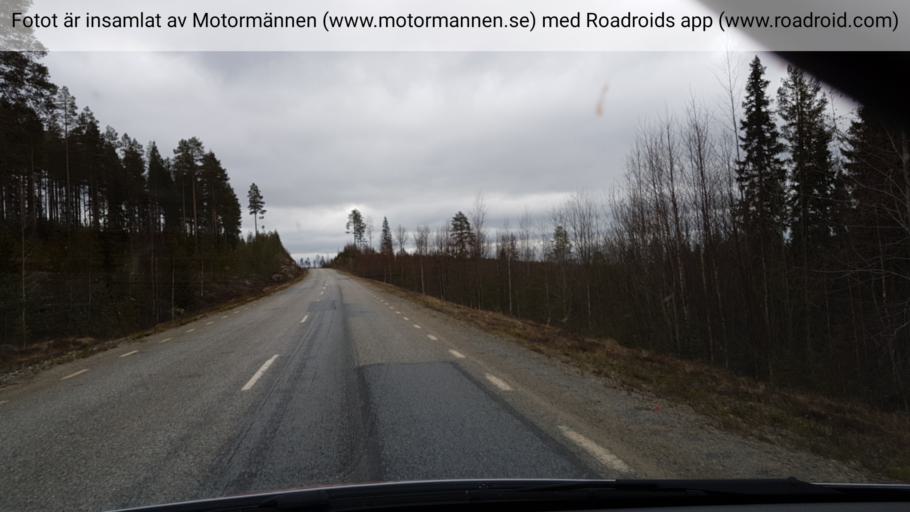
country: SE
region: Vaesternorrland
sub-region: OErnskoeldsviks Kommun
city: Bredbyn
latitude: 63.9130
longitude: 18.4859
